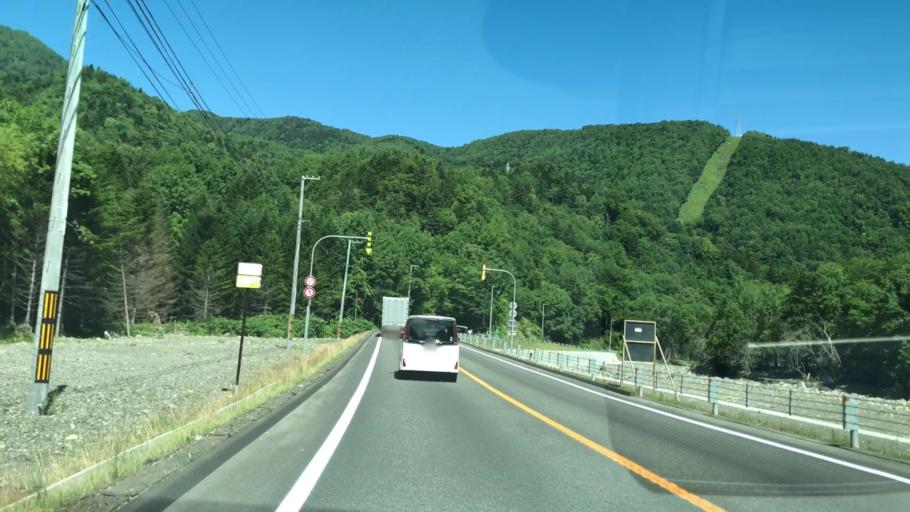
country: JP
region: Hokkaido
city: Shimo-furano
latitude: 42.9281
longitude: 142.5938
